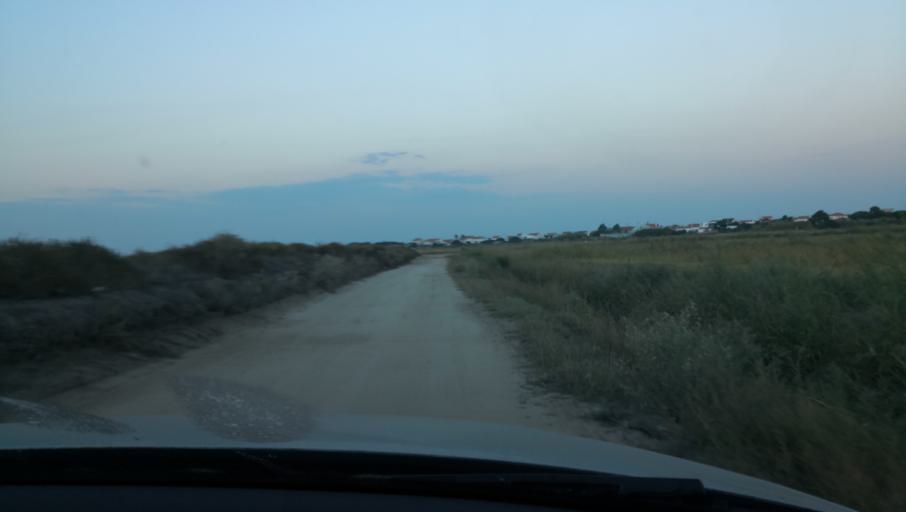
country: PT
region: Setubal
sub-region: Setubal
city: Setubal
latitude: 38.4075
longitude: -8.7606
